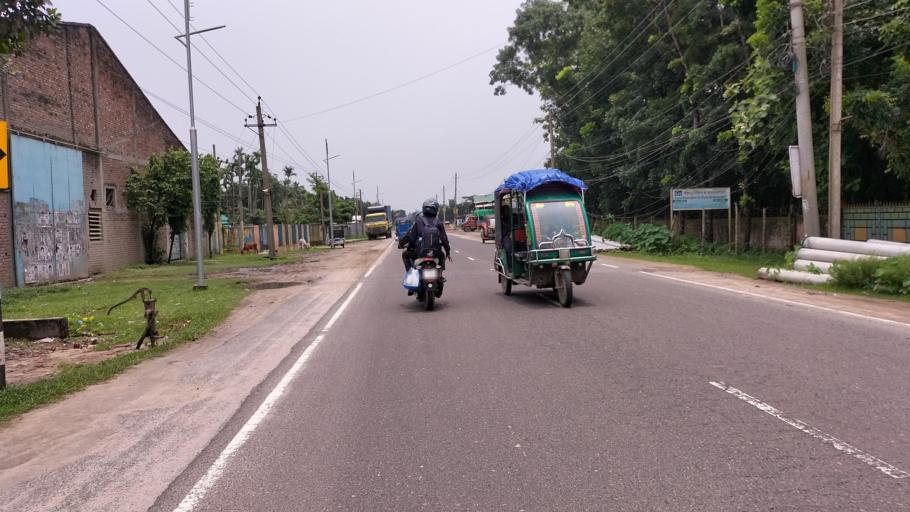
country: BD
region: Dhaka
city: Mymensingh
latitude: 24.7734
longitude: 90.4591
